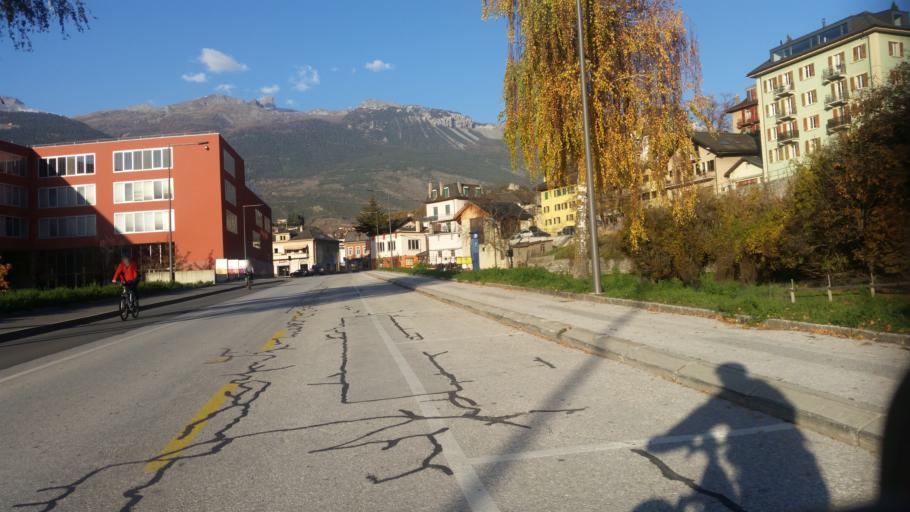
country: CH
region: Valais
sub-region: Sierre District
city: Sierre
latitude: 46.2923
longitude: 7.5367
